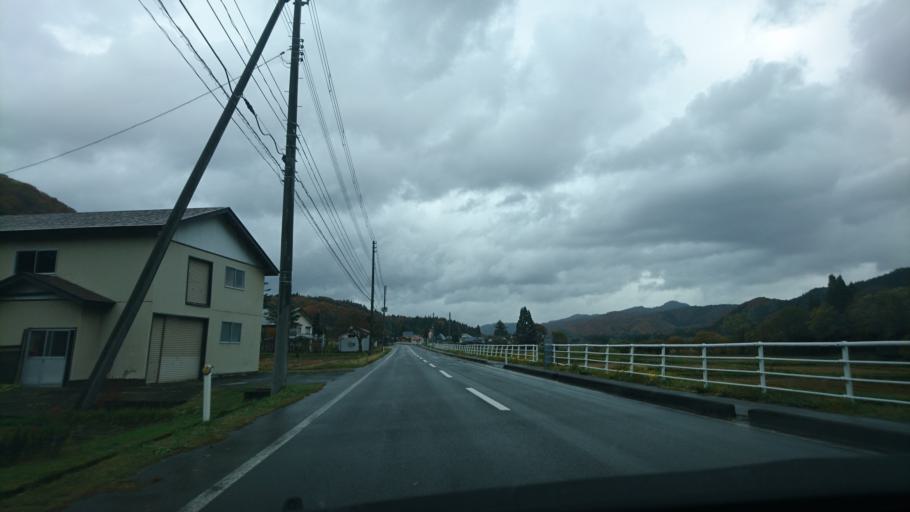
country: JP
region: Akita
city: Kakunodatemachi
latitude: 39.4836
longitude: 140.8044
